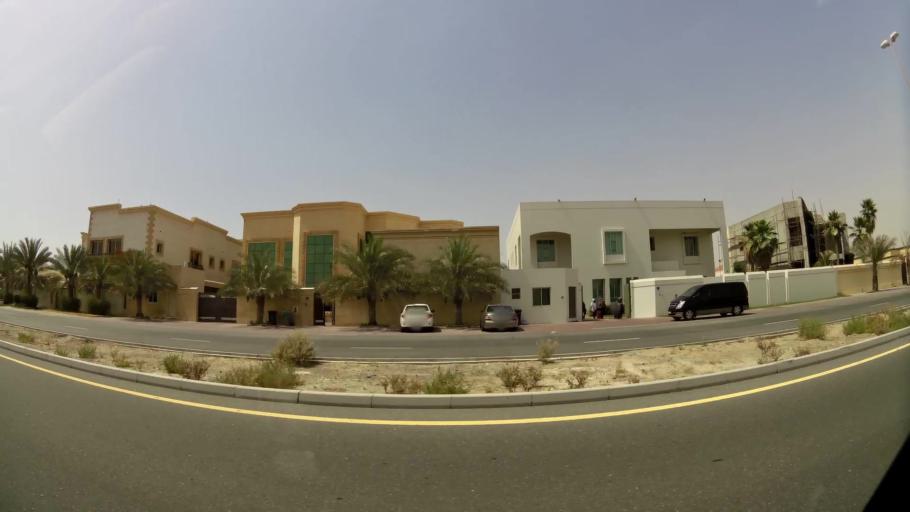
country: AE
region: Ash Shariqah
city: Sharjah
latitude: 25.2481
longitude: 55.4280
